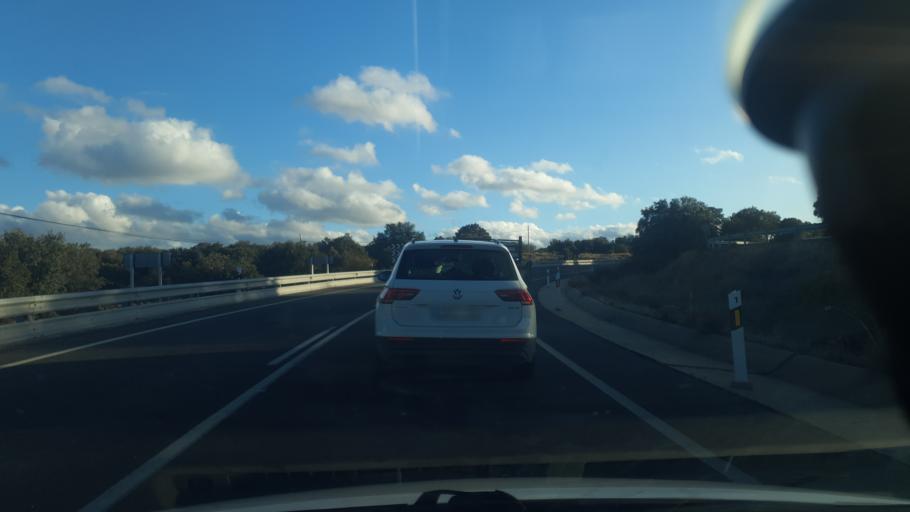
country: ES
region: Castille and Leon
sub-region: Provincia de Avila
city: Mingorria
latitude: 40.7205
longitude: -4.6730
